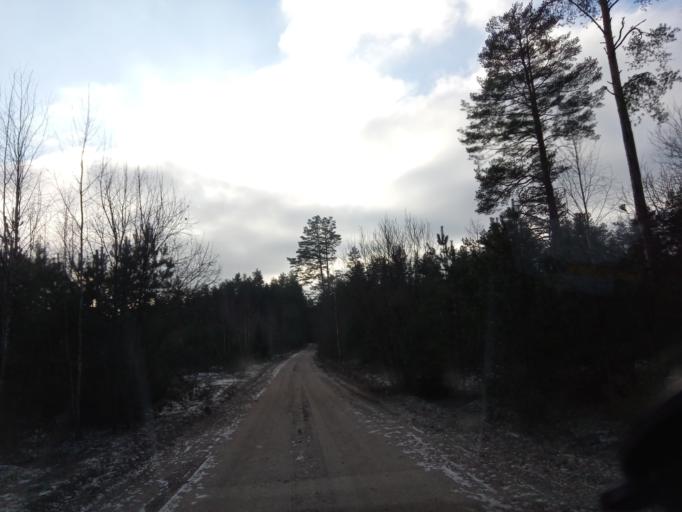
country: LT
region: Alytaus apskritis
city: Varena
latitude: 53.9825
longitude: 24.3347
